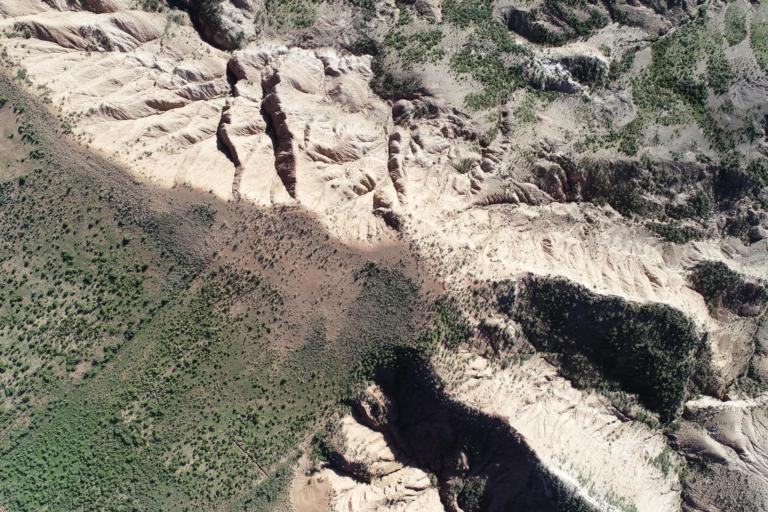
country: BO
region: La Paz
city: Curahuara de Carangas
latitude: -17.3028
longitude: -68.4972
